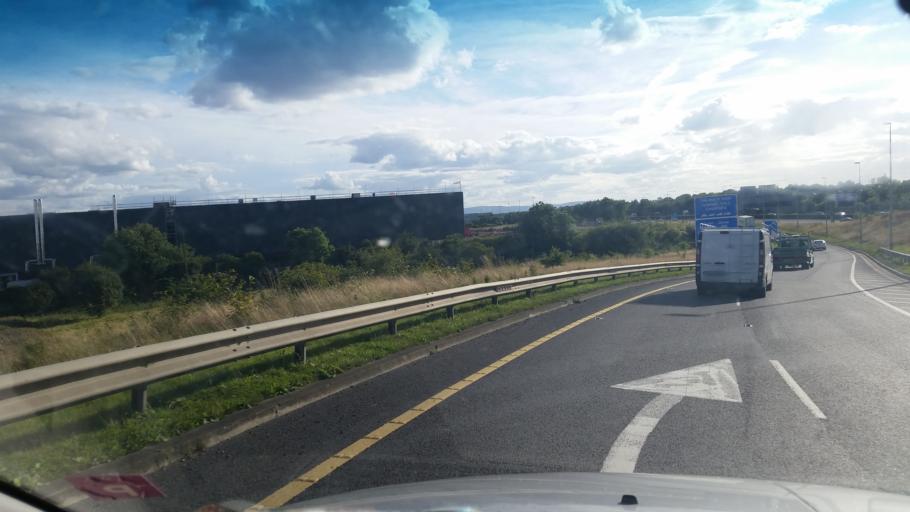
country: IE
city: Bonnybrook
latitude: 53.4089
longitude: -6.2249
